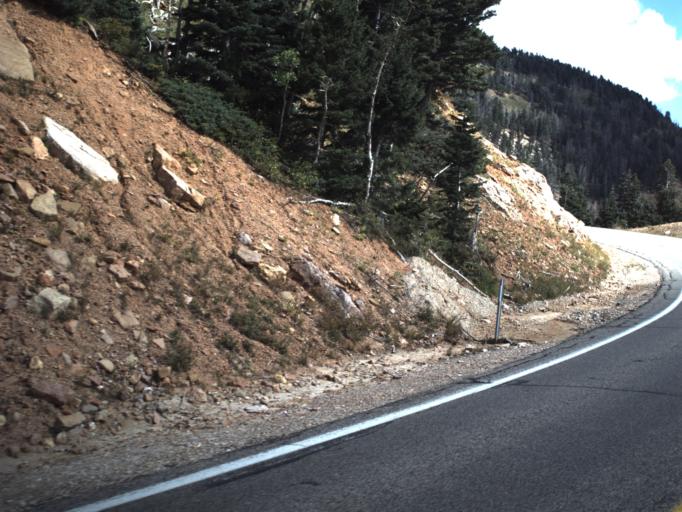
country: US
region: Utah
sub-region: Iron County
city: Cedar City
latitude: 37.5775
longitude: -112.8691
